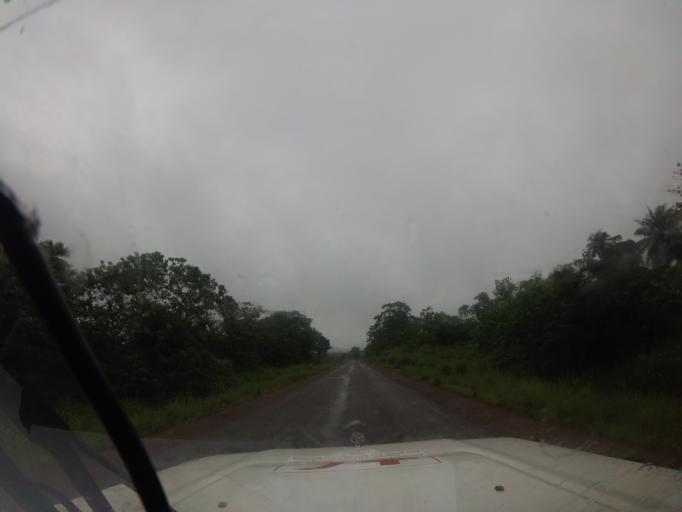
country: SL
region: Northern Province
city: Binkolo
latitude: 8.9283
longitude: -12.0111
